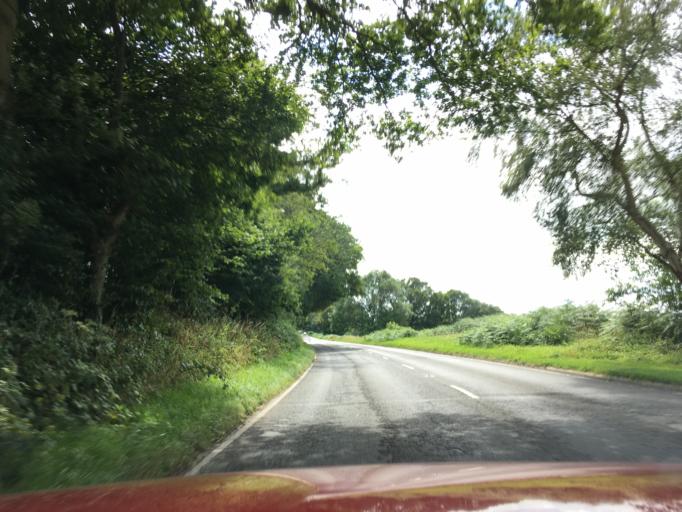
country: GB
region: England
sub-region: East Sussex
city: Crowborough
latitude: 51.1081
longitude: 0.1537
